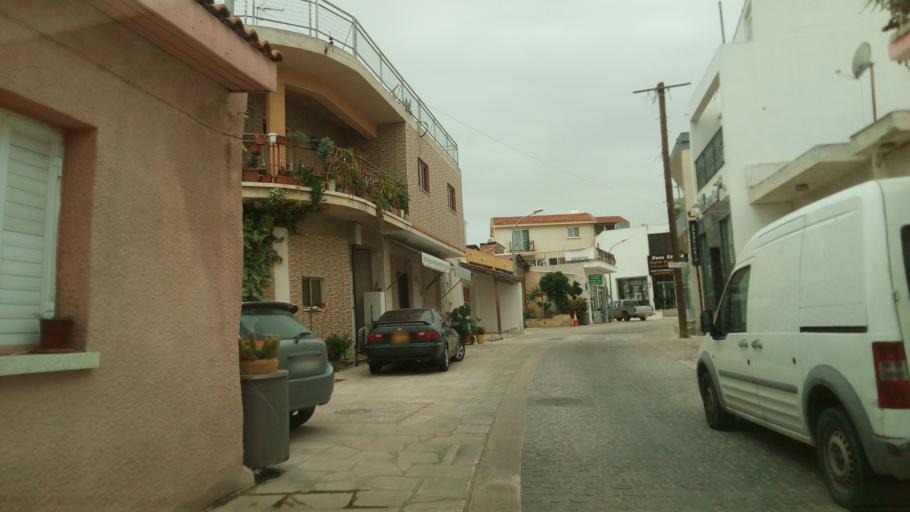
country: CY
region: Larnaka
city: Kornos
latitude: 34.9240
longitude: 33.3976
